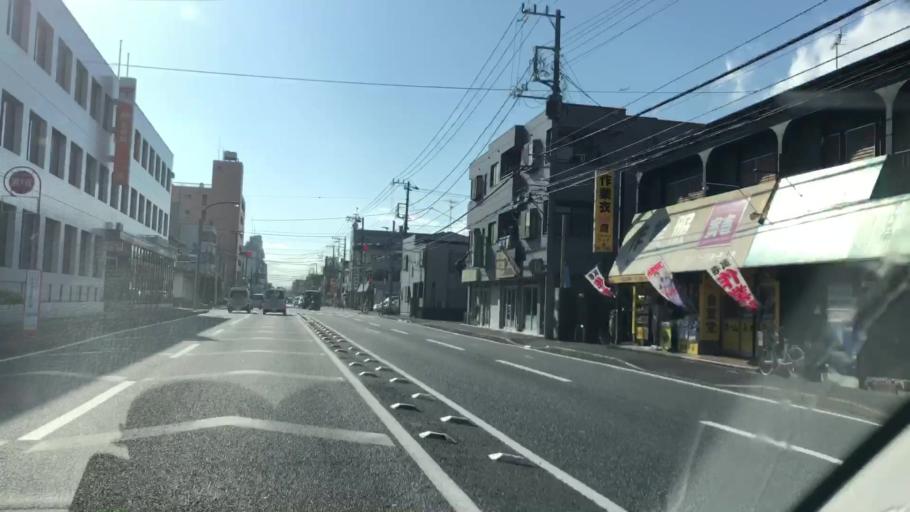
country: JP
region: Tokyo
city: Urayasu
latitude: 35.6810
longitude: 139.9074
